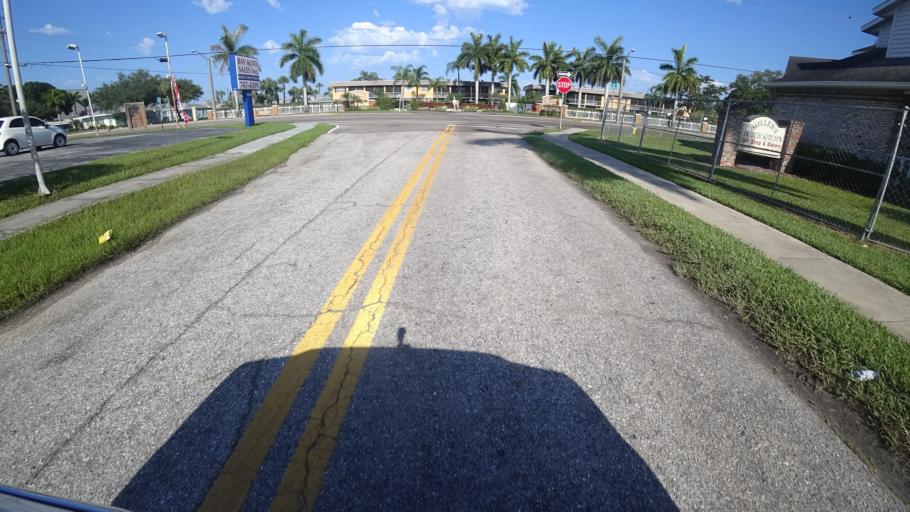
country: US
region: Florida
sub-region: Manatee County
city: South Bradenton
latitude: 27.4701
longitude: -82.5749
